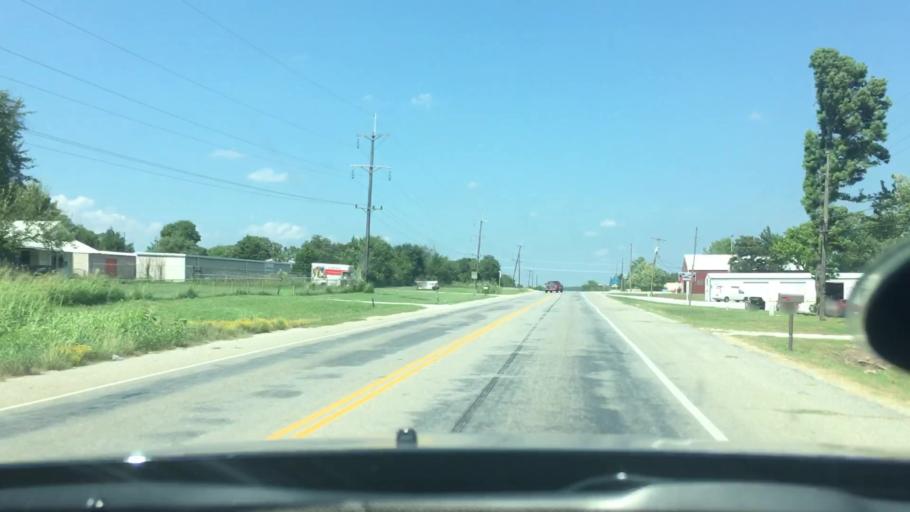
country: US
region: Oklahoma
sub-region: Pontotoc County
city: Byng
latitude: 34.8212
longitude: -96.6786
